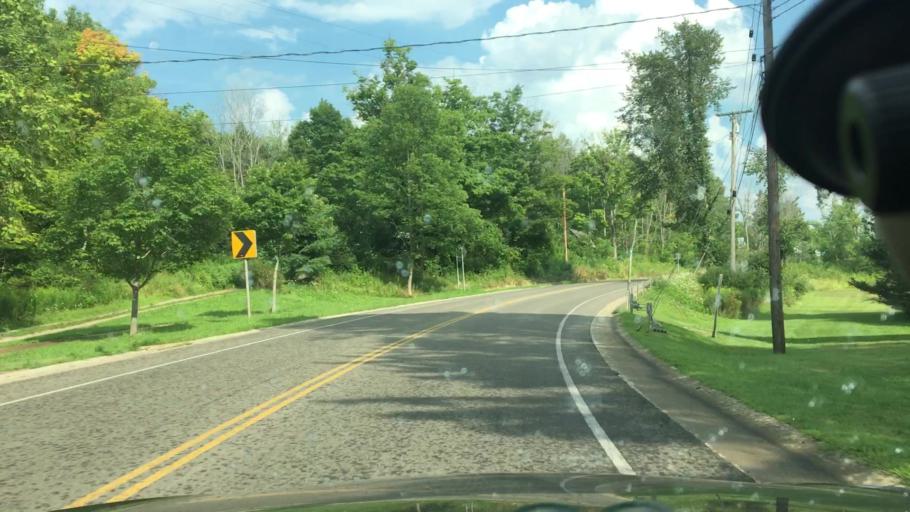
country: US
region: New York
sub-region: Cattaraugus County
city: Randolph
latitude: 42.1724
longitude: -78.9417
